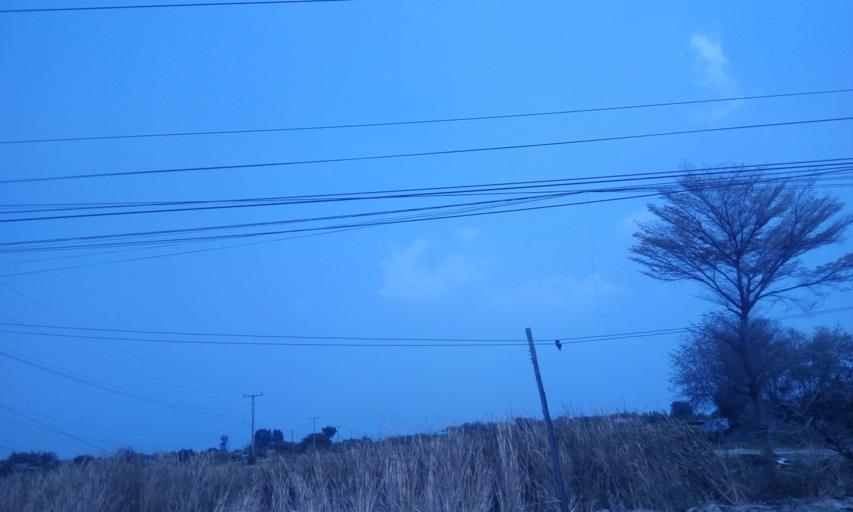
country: TH
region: Chachoengsao
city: Ban Pho
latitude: 13.5961
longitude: 101.1193
